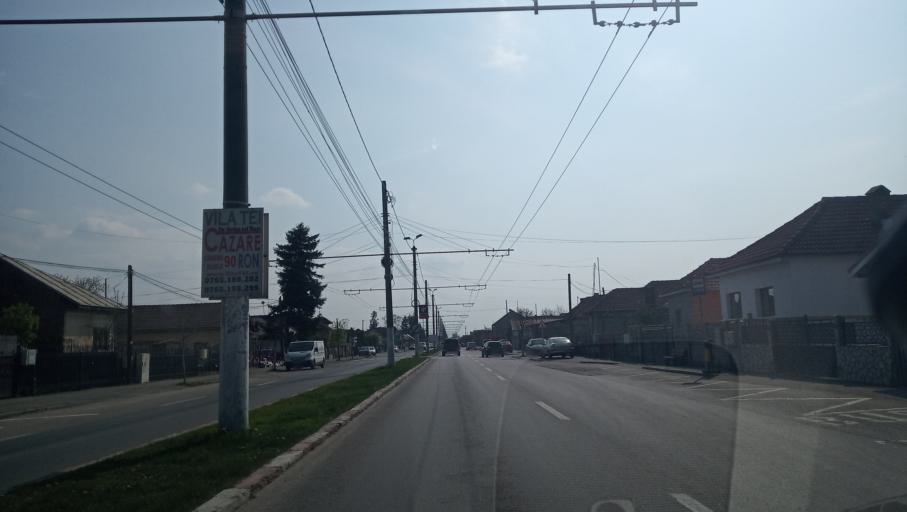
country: RO
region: Gorj
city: Targu Jiu
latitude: 45.0630
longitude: 23.2910
